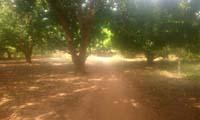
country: ML
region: Bamako
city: Bamako
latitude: 12.5831
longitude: -8.0824
